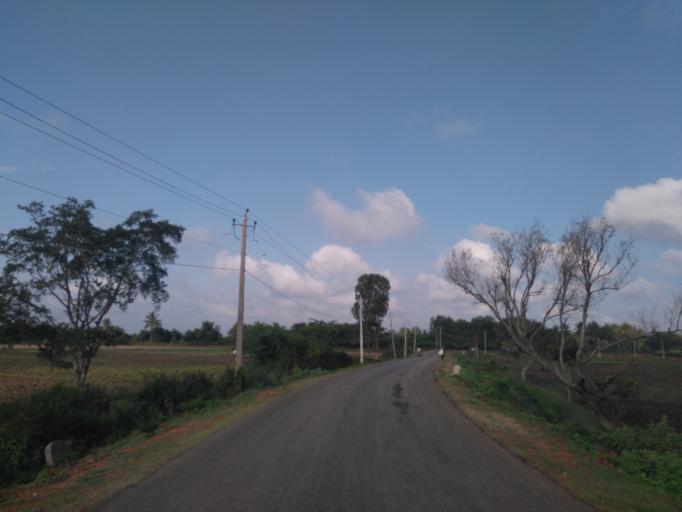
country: IN
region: Karnataka
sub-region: Mysore
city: Tirumakudal Narsipur
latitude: 12.2571
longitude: 76.9919
